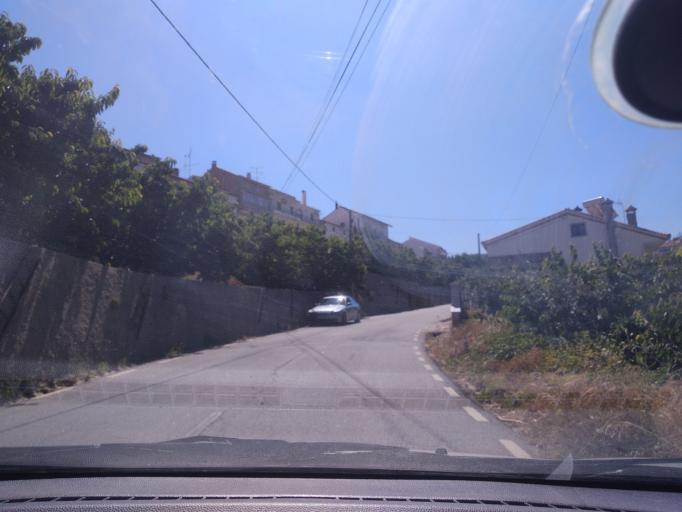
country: PT
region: Castelo Branco
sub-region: Concelho do Fundao
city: Fundao
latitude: 40.1208
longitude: -7.4854
